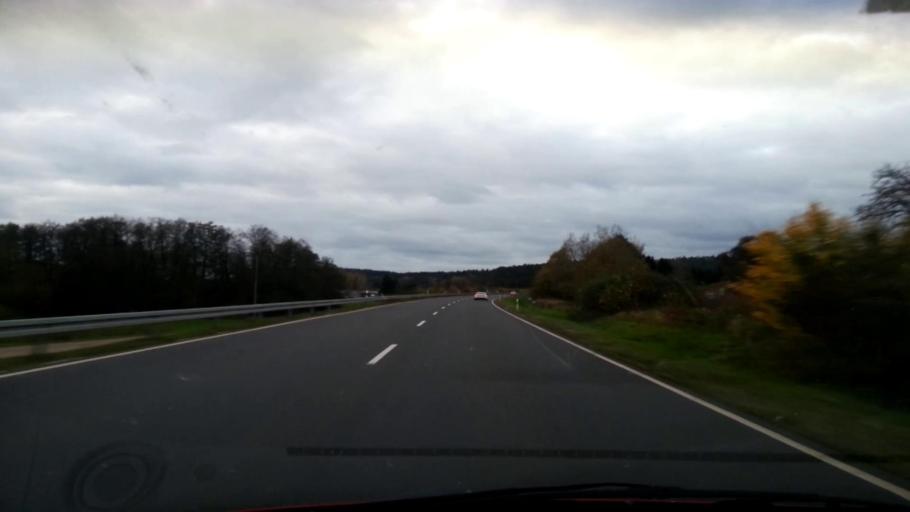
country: DE
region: Bavaria
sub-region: Upper Franconia
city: Schneckenlohe
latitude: 50.2145
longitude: 11.2019
